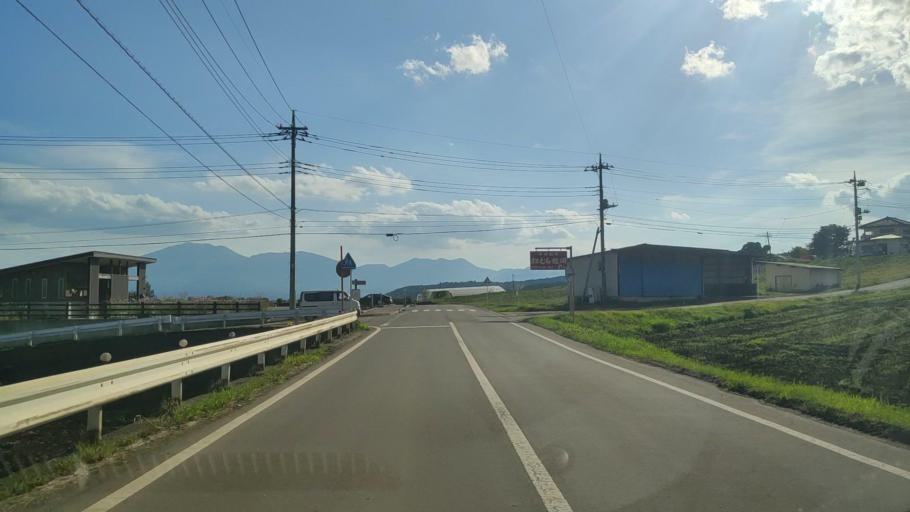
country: JP
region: Nagano
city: Suzaka
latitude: 36.5779
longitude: 138.5641
